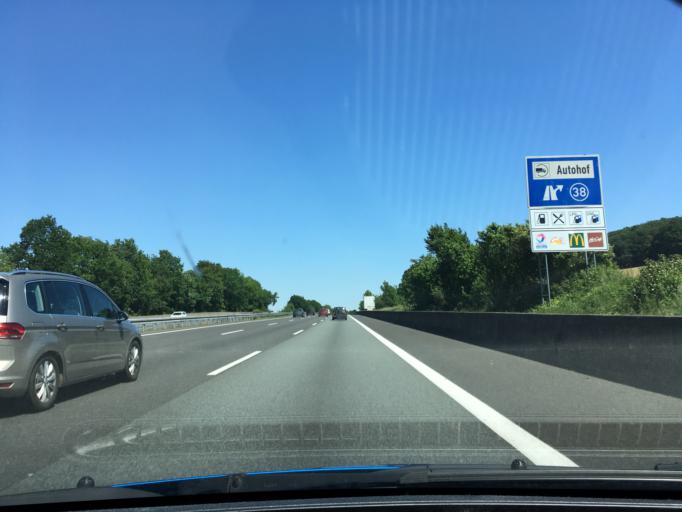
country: DE
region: Lower Saxony
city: Bad Nenndorf
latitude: 52.3170
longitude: 9.3839
